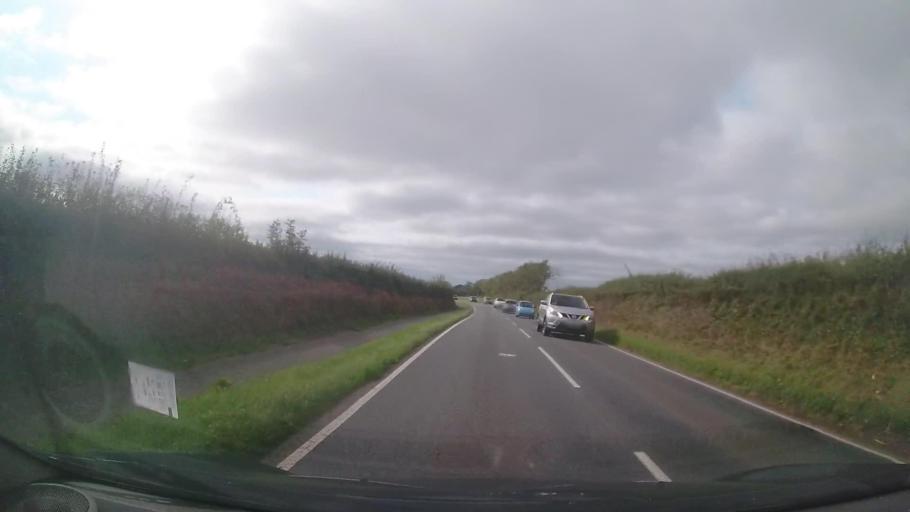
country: GB
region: Wales
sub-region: Pembrokeshire
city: Steynton
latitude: 51.7316
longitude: -4.9960
